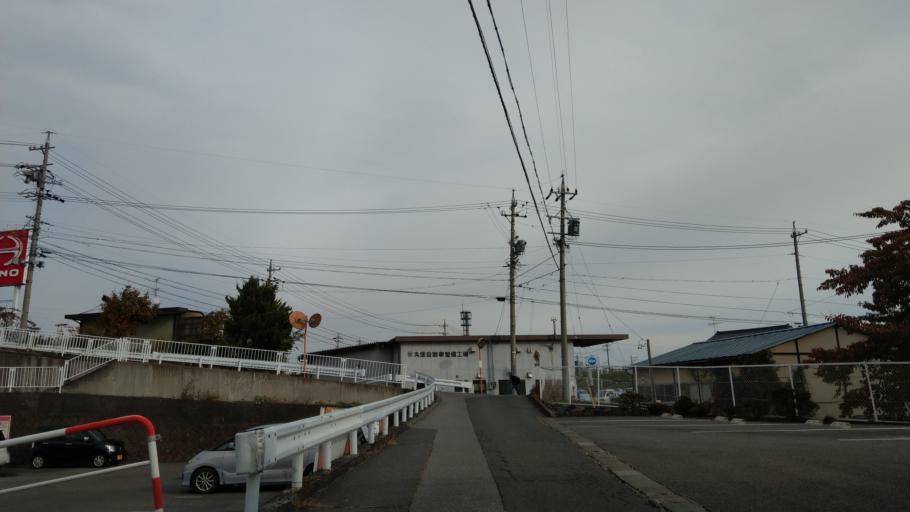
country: JP
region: Nagano
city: Komoro
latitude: 36.3179
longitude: 138.4405
